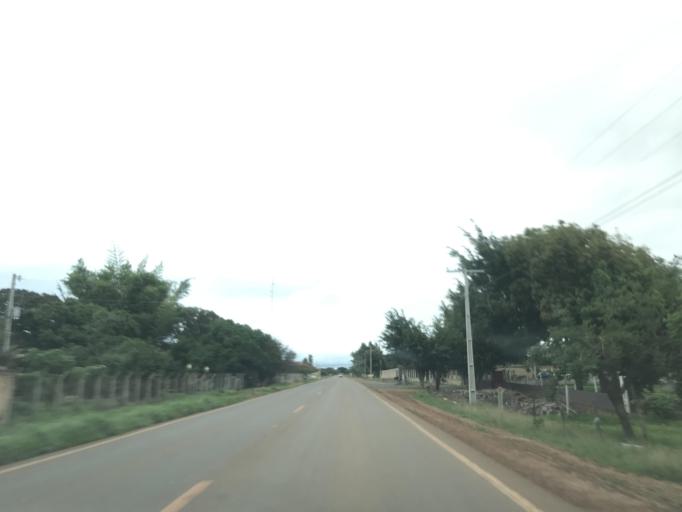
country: BR
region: Goias
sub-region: Luziania
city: Luziania
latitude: -16.3331
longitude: -48.0190
